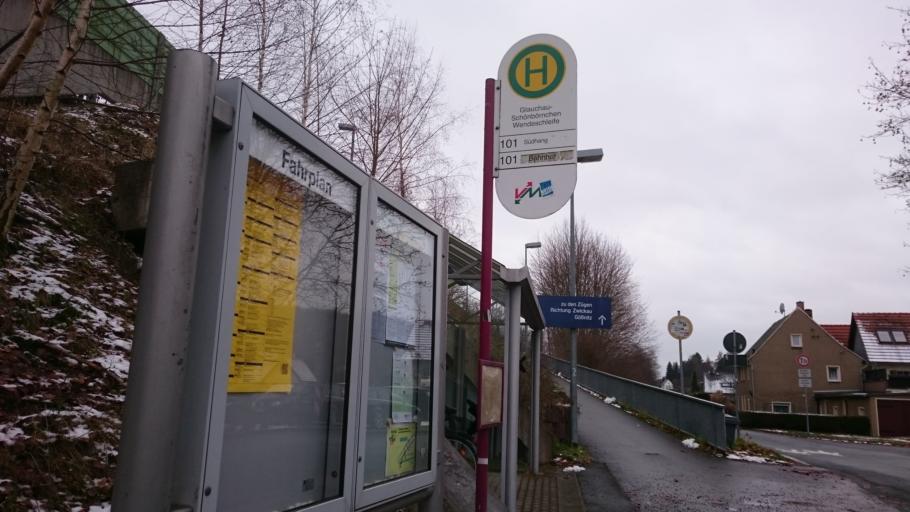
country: DE
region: Saxony
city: Dennheritz
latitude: 50.8224
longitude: 12.5023
